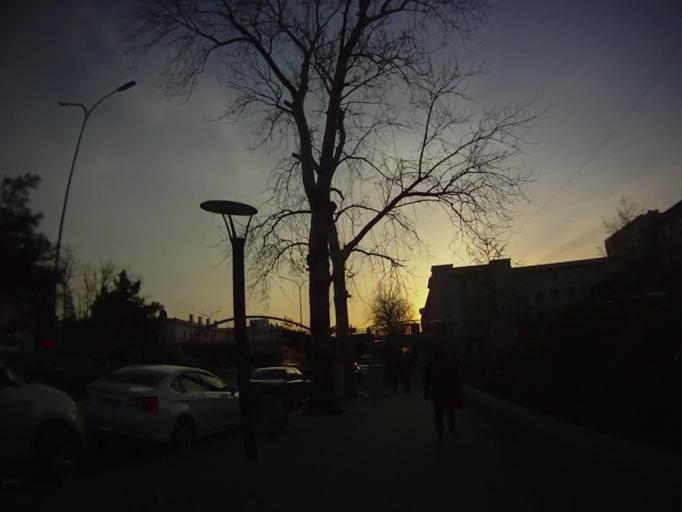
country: CN
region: Beijing
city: Longtan
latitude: 39.8829
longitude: 116.4224
